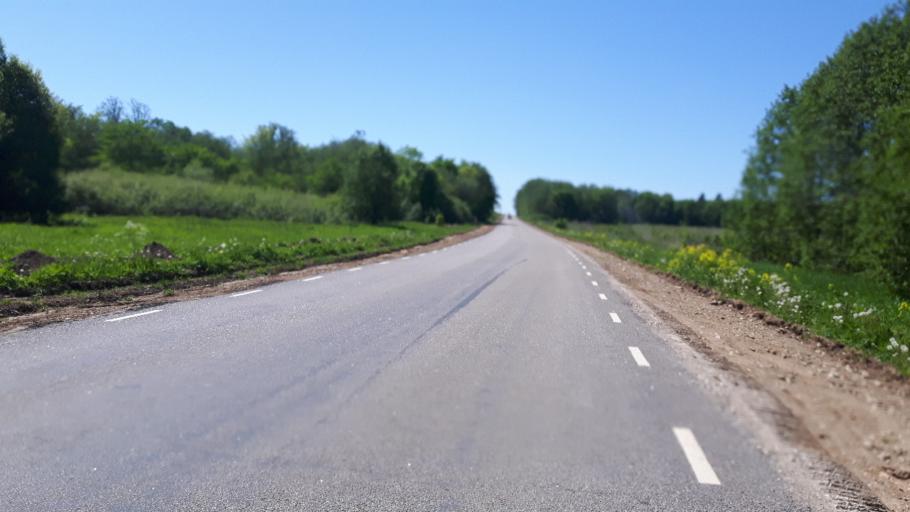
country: EE
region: Ida-Virumaa
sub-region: Narva-Joesuu linn
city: Narva-Joesuu
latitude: 59.4082
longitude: 27.9434
